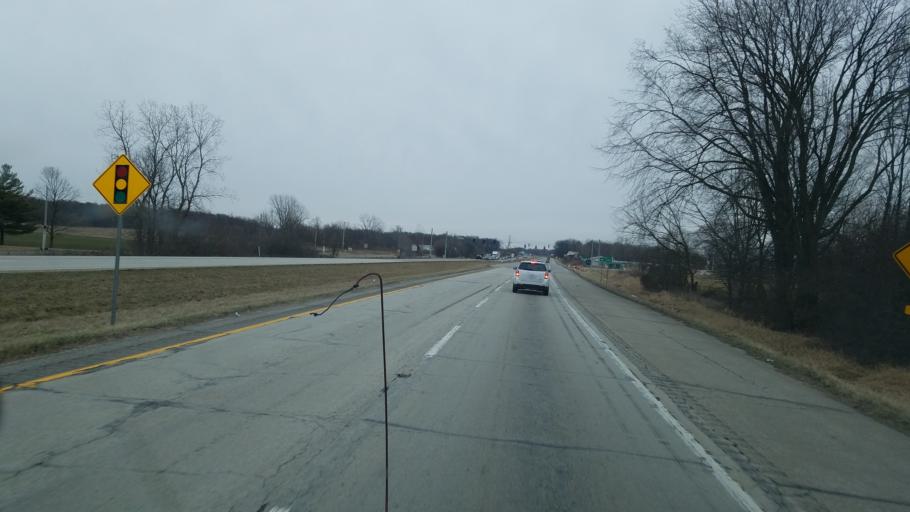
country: US
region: Indiana
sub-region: Marshall County
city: Plymouth
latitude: 41.3639
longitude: -86.3800
